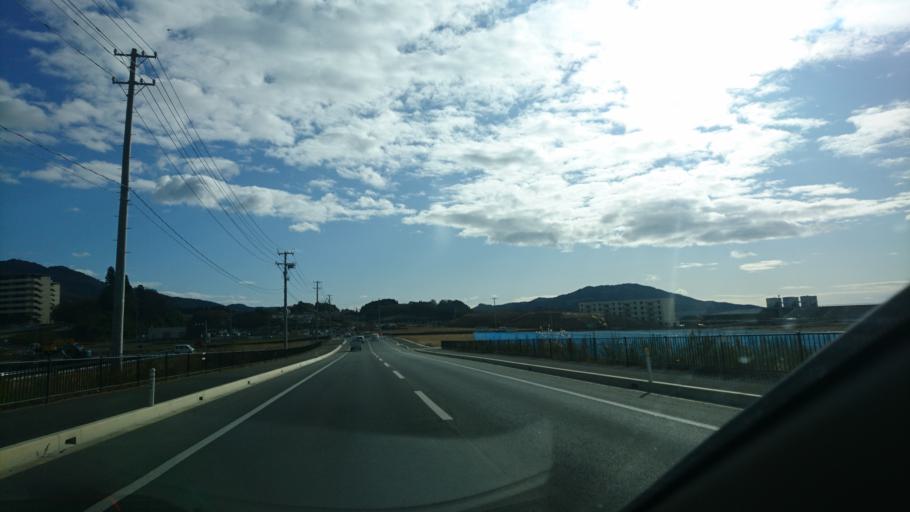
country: JP
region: Iwate
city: Ofunato
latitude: 39.0118
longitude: 141.6418
